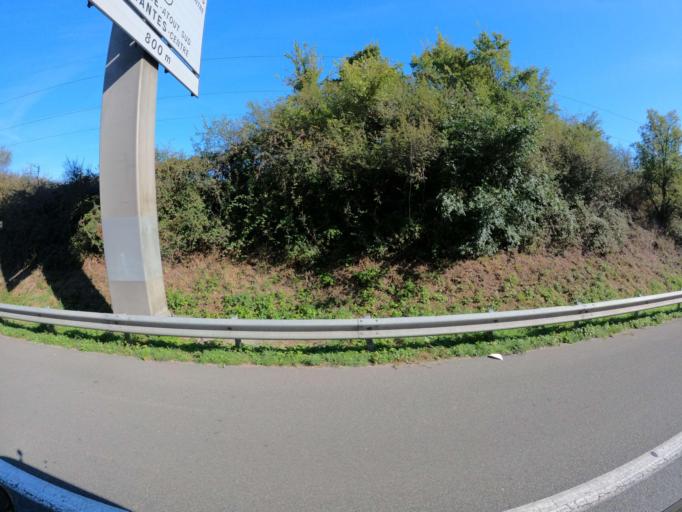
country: FR
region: Pays de la Loire
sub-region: Departement de la Loire-Atlantique
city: Bouguenais
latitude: 47.1771
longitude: -1.5992
